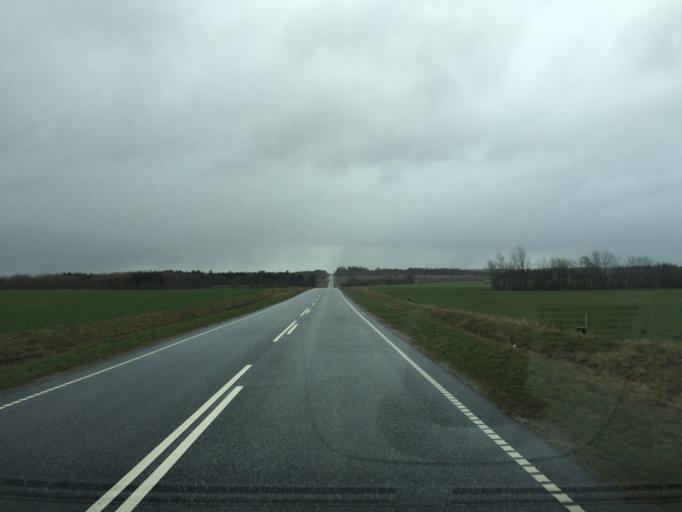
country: DK
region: Central Jutland
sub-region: Ringkobing-Skjern Kommune
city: Videbaek
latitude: 56.1871
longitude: 8.6221
